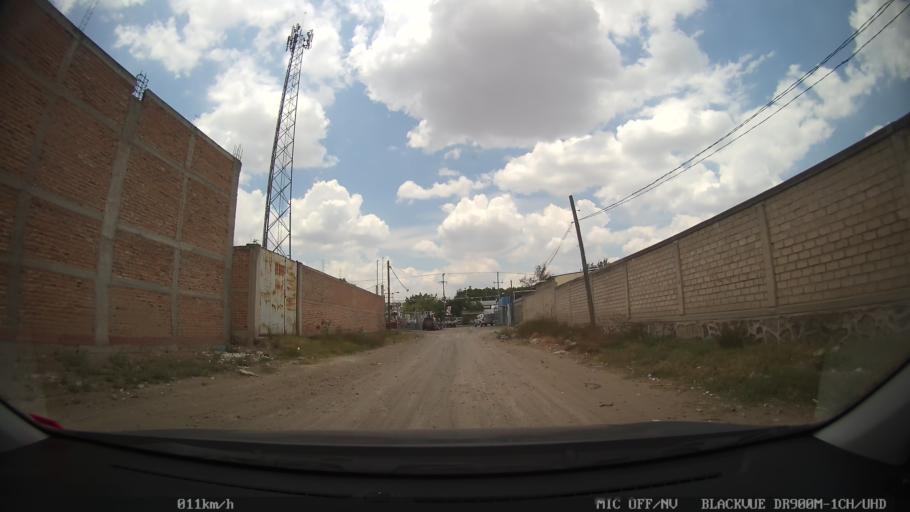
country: MX
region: Jalisco
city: Tonala
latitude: 20.6533
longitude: -103.2333
